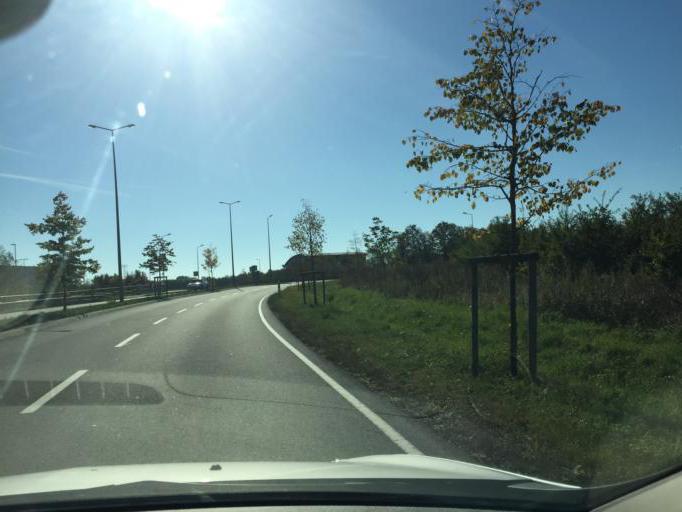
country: LU
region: Luxembourg
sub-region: Canton de Luxembourg
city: Contern
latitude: 49.5947
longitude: 6.2153
